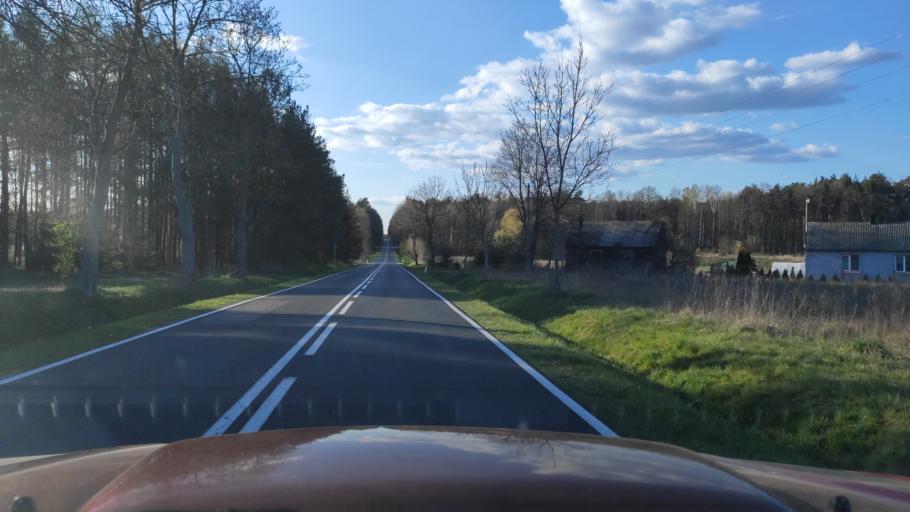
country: PL
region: Masovian Voivodeship
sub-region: Powiat zwolenski
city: Zwolen
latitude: 51.3845
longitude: 21.5561
